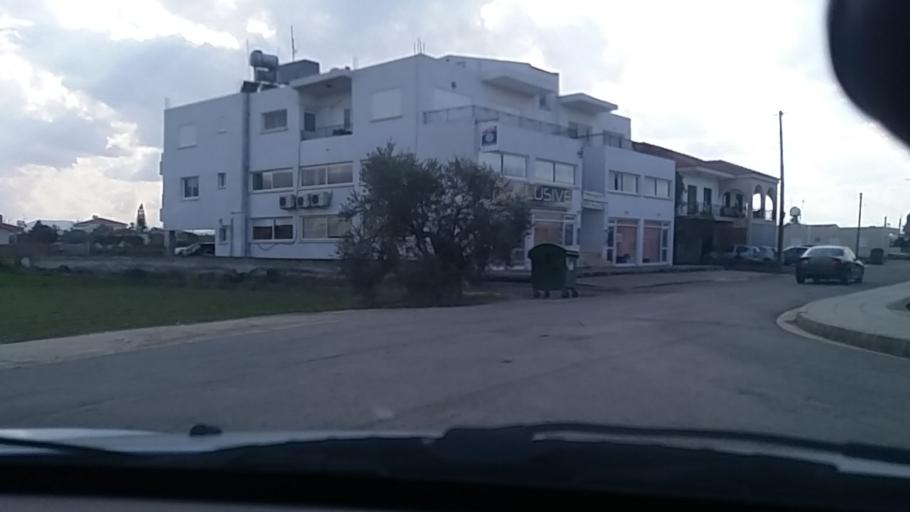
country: CY
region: Lefkosia
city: Akaki
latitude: 35.1371
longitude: 33.1323
